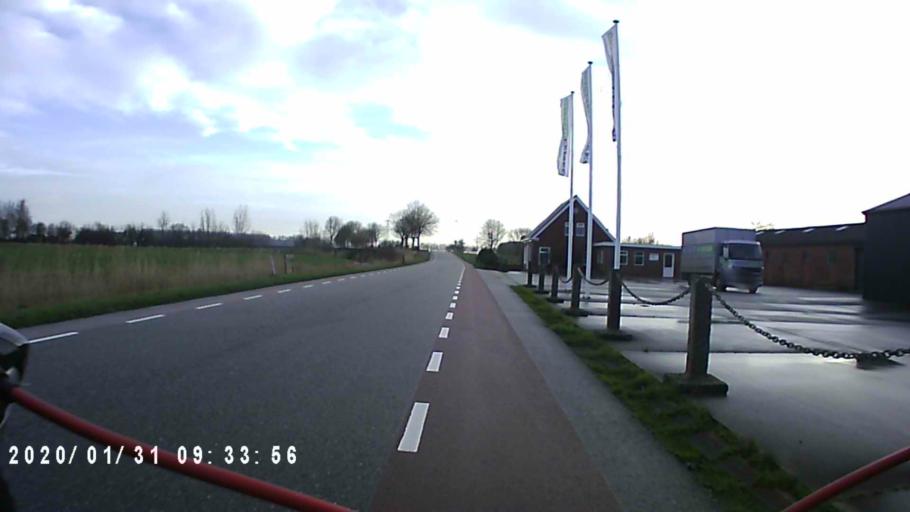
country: NL
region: Groningen
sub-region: Gemeente Winsum
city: Winsum
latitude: 53.3063
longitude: 6.4770
